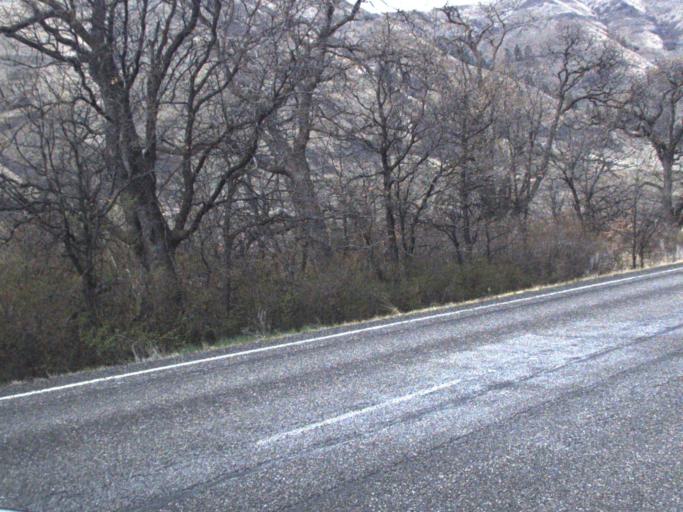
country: US
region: Washington
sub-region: Yakima County
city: Tieton
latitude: 46.7504
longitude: -120.8116
